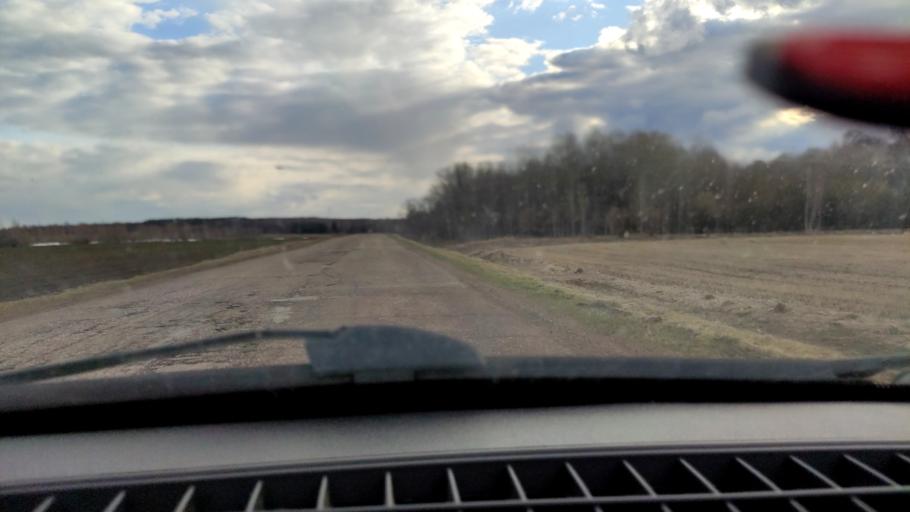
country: RU
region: Bashkortostan
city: Karmaskaly
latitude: 54.3243
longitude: 55.9866
